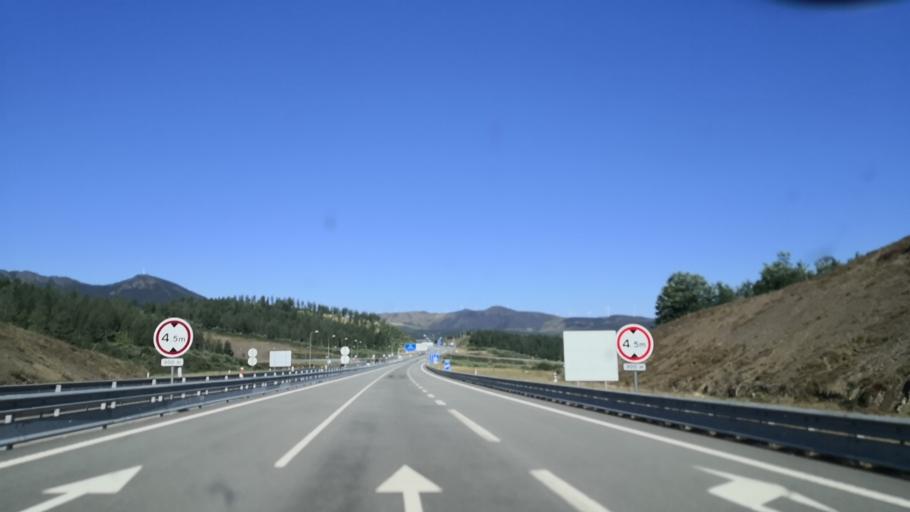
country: PT
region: Vila Real
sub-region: Santa Marta de Penaguiao
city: Santa Marta de Penaguiao
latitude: 41.2787
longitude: -7.8277
